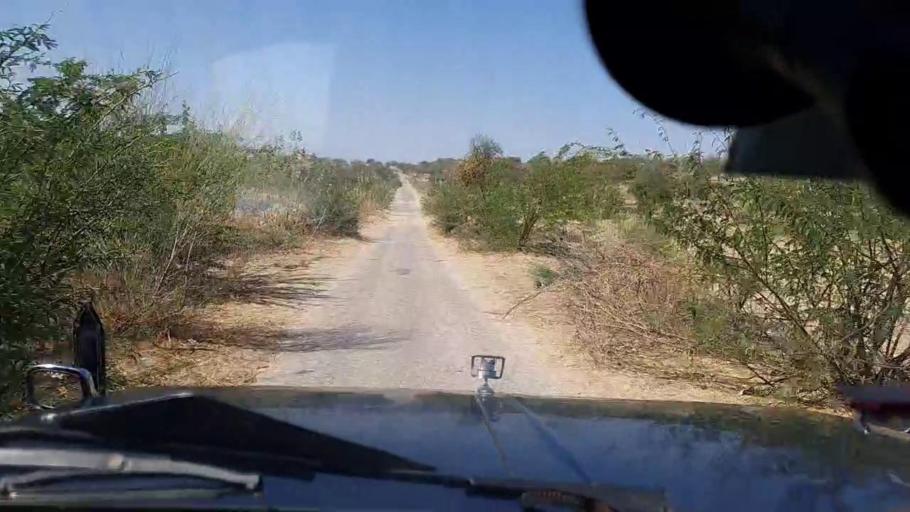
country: PK
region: Sindh
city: Mithi
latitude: 24.6118
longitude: 69.7054
